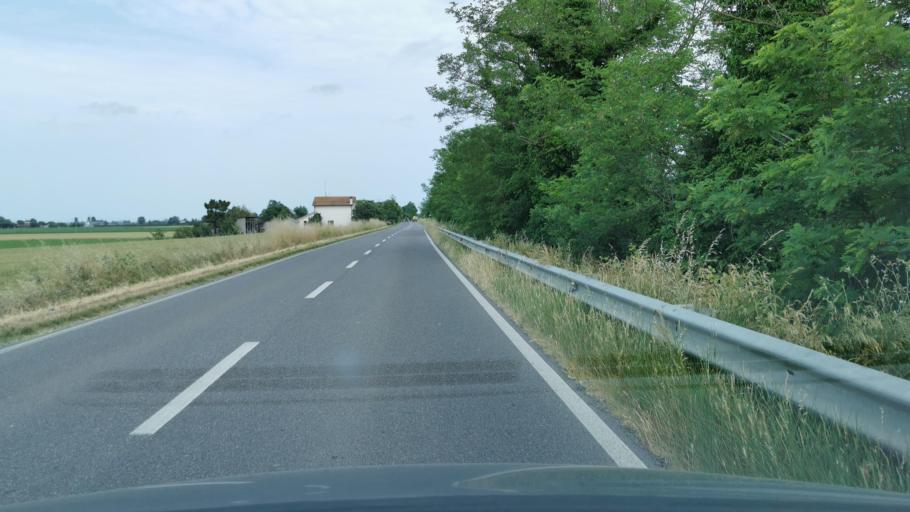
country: IT
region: Emilia-Romagna
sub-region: Provincia di Ravenna
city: Sant'Alberto
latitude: 44.5411
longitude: 12.1950
